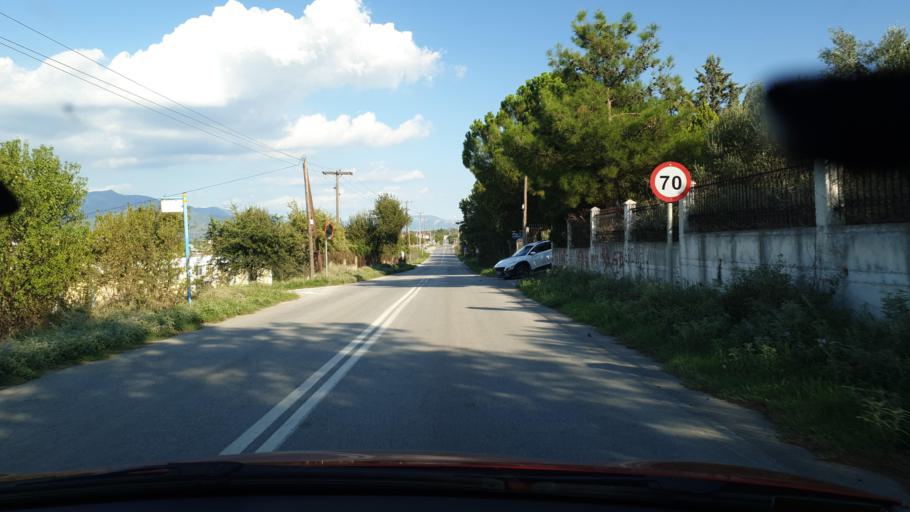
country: GR
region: Central Macedonia
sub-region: Nomos Thessalonikis
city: Agia Paraskevi
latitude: 40.4831
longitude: 23.0571
